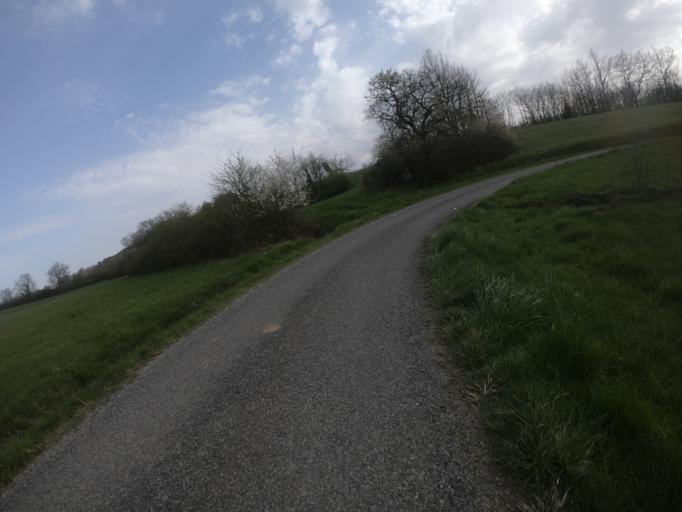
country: FR
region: Languedoc-Roussillon
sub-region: Departement de l'Aude
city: Belpech
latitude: 43.1279
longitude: 1.7441
